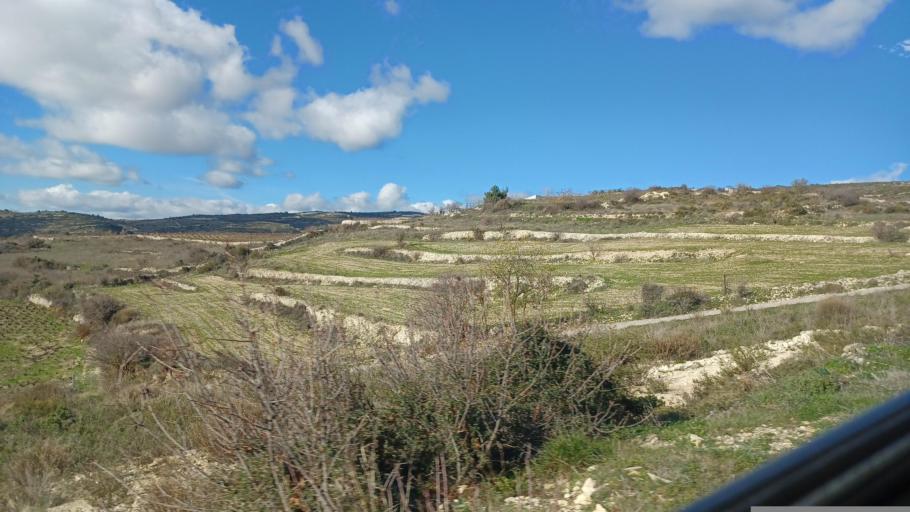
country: CY
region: Limassol
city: Pachna
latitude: 34.8382
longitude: 32.8003
